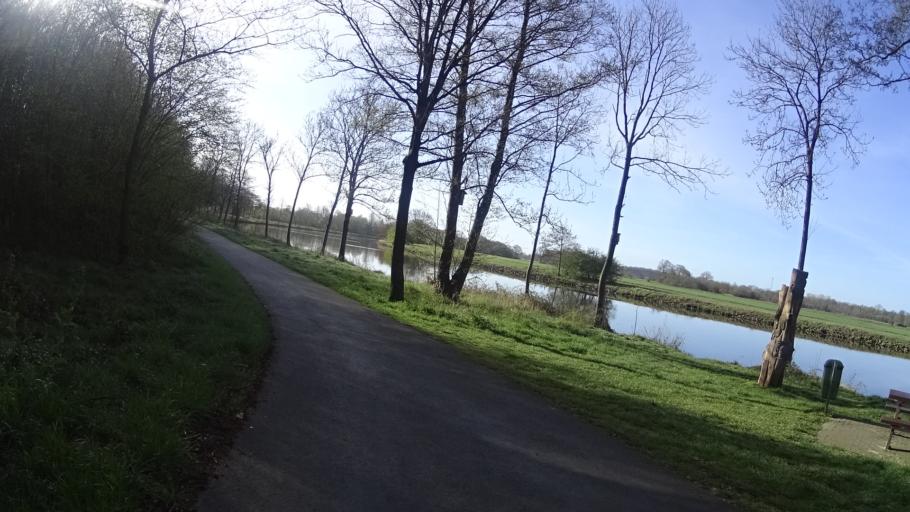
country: DE
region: Lower Saxony
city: Haren
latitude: 52.8076
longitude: 7.2560
